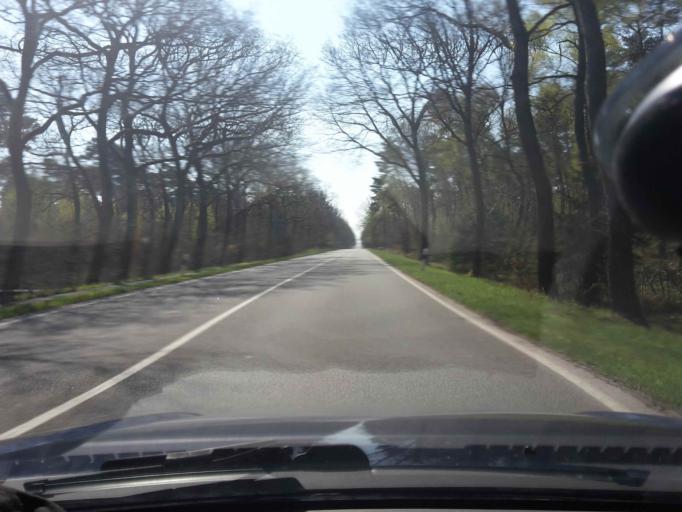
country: DE
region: Lower Saxony
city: Schneverdingen
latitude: 53.1261
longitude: 9.8475
